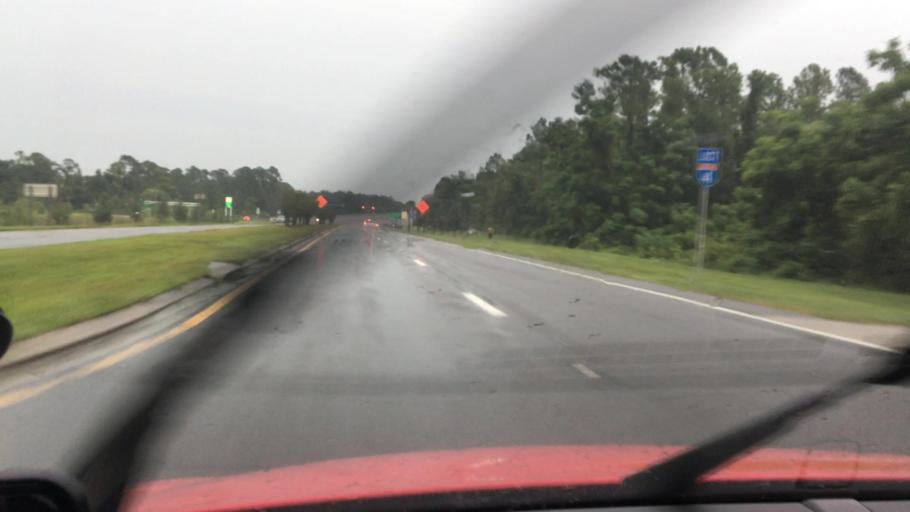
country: US
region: Florida
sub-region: Volusia County
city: Lake Helen
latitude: 29.0160
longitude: -81.2390
